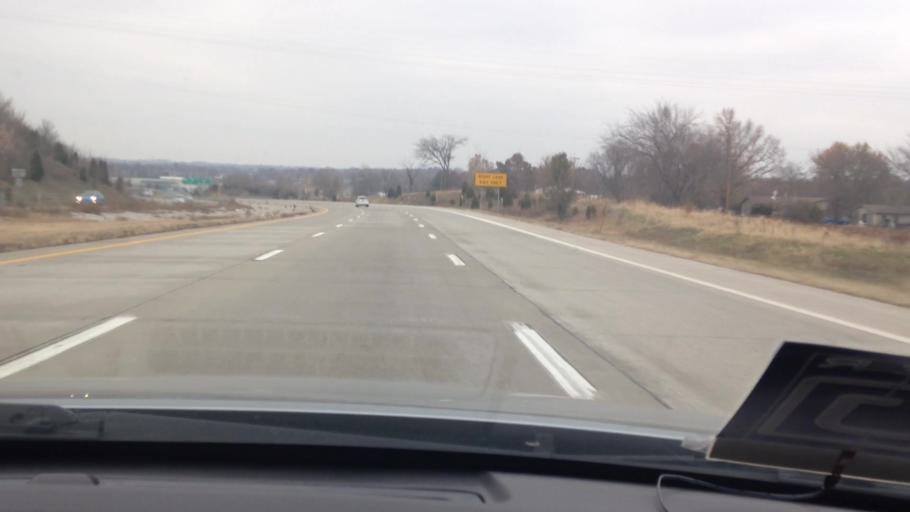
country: US
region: Missouri
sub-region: Cass County
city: Harrisonville
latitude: 38.6312
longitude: -94.3507
